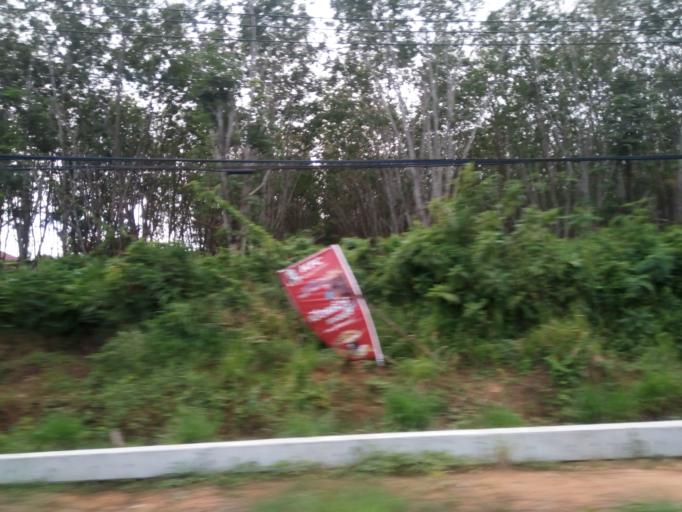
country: TH
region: Phuket
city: Mueang Phuket
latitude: 7.8472
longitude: 98.3824
